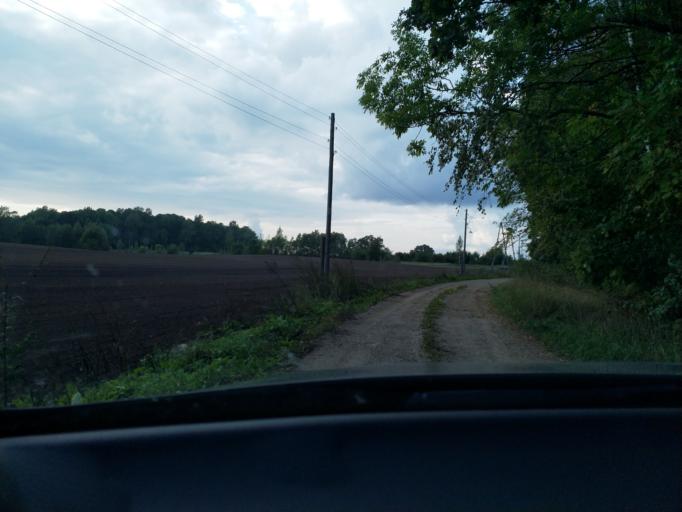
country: LV
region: Kuldigas Rajons
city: Kuldiga
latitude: 56.8556
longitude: 21.8150
